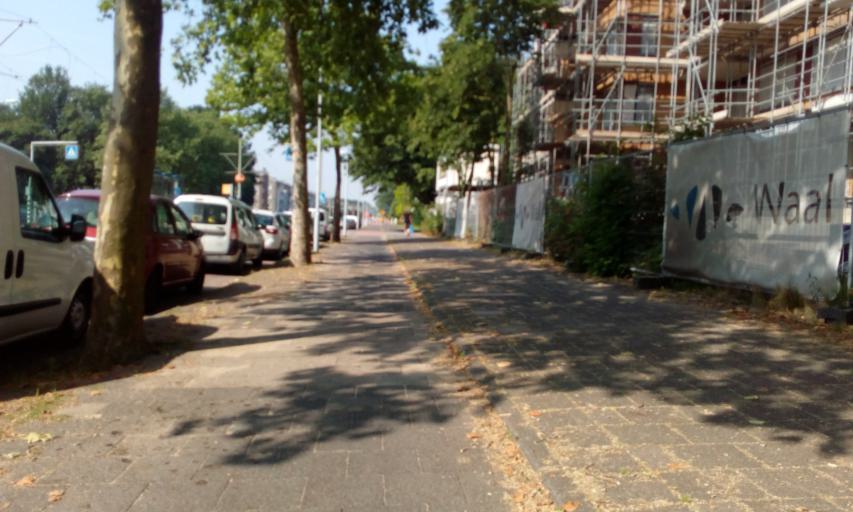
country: NL
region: South Holland
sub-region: Gemeente Leidschendam-Voorburg
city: Voorburg
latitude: 52.0797
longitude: 4.3609
